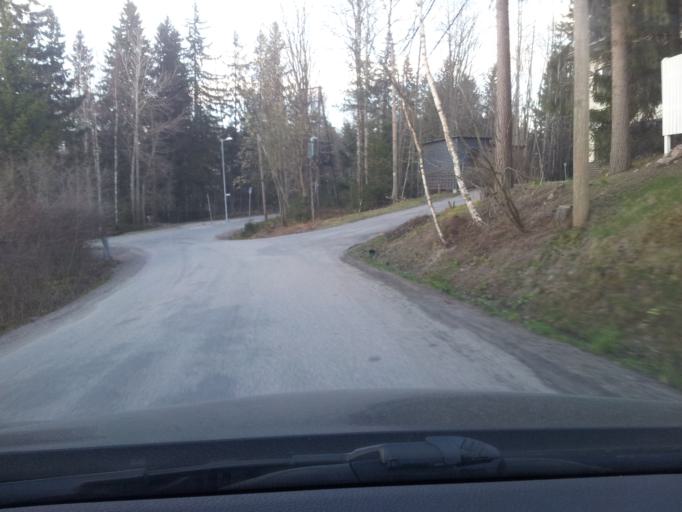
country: FI
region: Uusimaa
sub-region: Helsinki
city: Espoo
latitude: 60.1530
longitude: 24.6725
